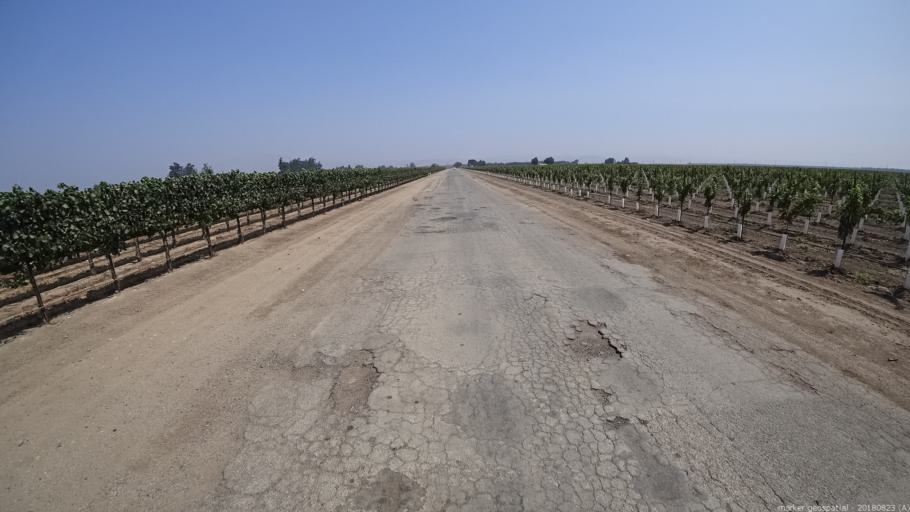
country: US
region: California
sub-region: Monterey County
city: Greenfield
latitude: 36.3053
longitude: -121.2721
